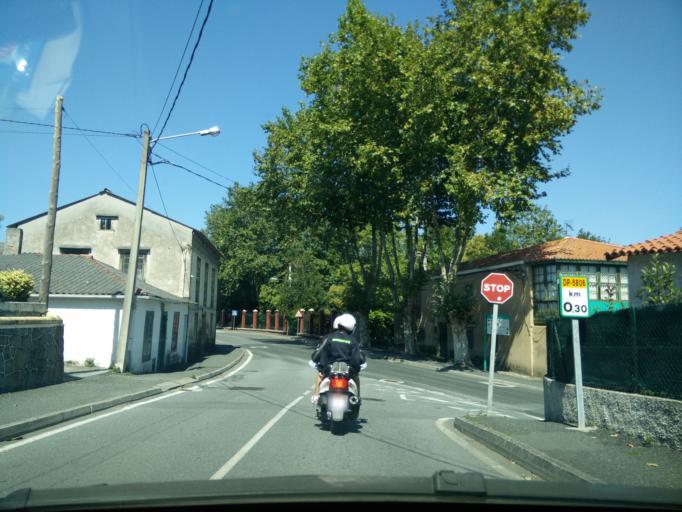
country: ES
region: Galicia
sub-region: Provincia da Coruna
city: Oleiros
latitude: 43.3461
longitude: -8.3426
